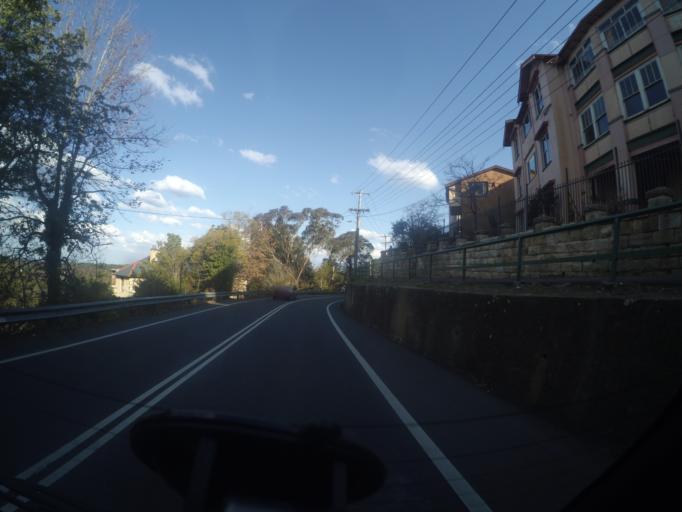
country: AU
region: New South Wales
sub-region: Blue Mountains Municipality
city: Katoomba
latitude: -33.7132
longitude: 150.3128
